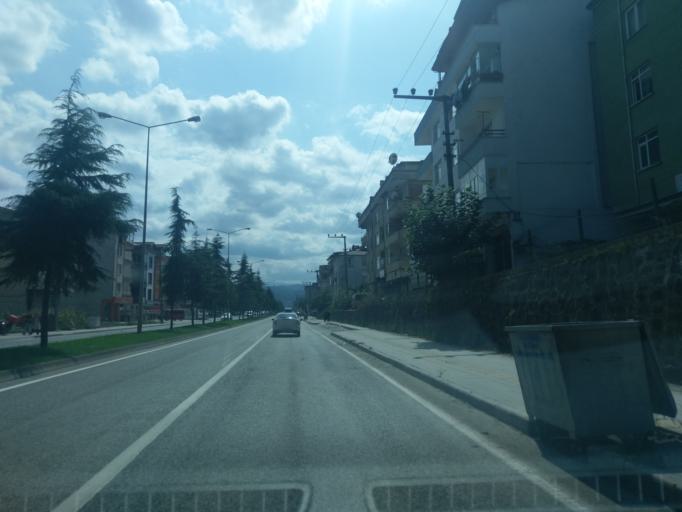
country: TR
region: Ordu
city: Ordu
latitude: 40.9625
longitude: 37.8989
